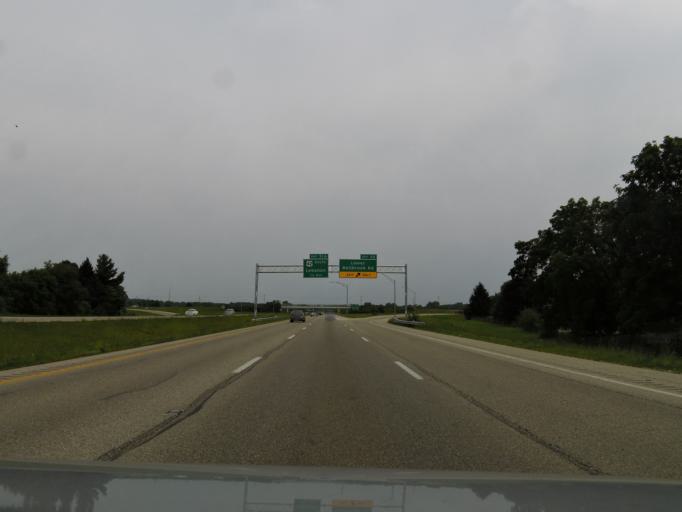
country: US
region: Ohio
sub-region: Greene County
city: Xenia
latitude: 39.6725
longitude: -83.9625
